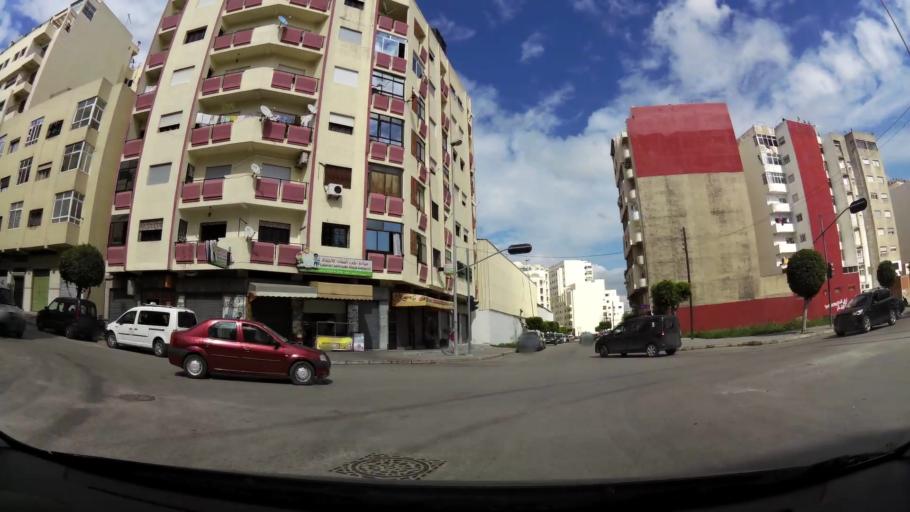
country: MA
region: Tanger-Tetouan
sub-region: Tanger-Assilah
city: Tangier
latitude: 35.7692
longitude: -5.8076
